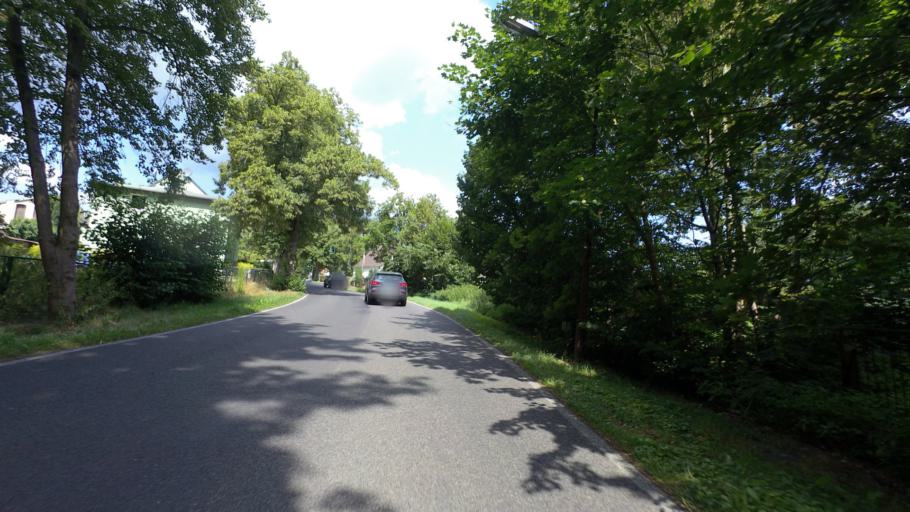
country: DE
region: Brandenburg
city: Teupitz
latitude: 52.1306
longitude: 13.5885
